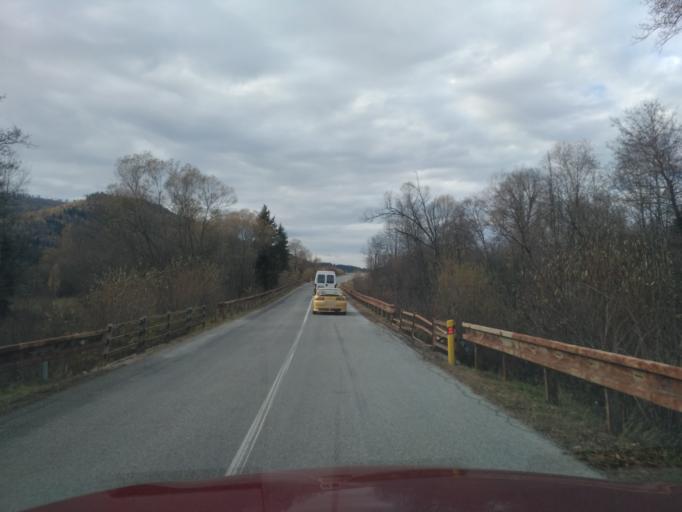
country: SK
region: Kosicky
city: Krompachy
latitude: 48.7978
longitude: 20.7480
